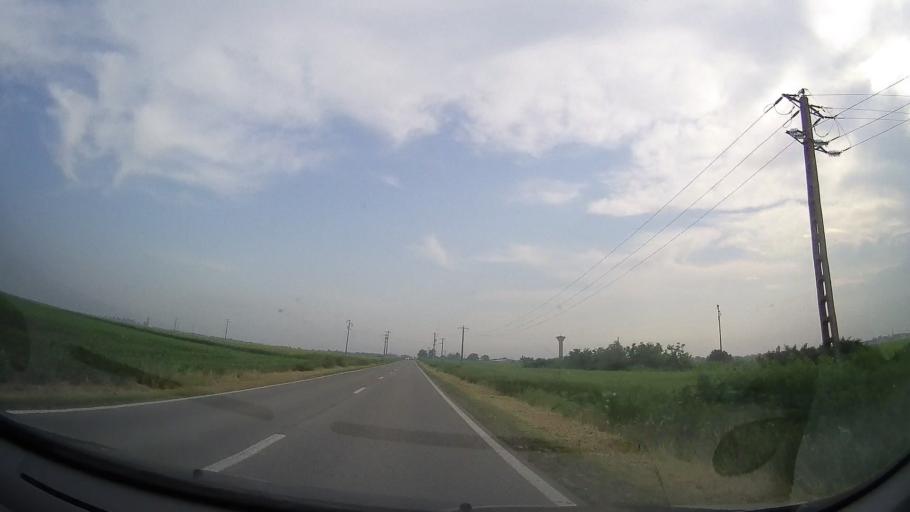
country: RO
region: Timis
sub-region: Comuna Parta
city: Parta
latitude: 45.6499
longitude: 21.1415
